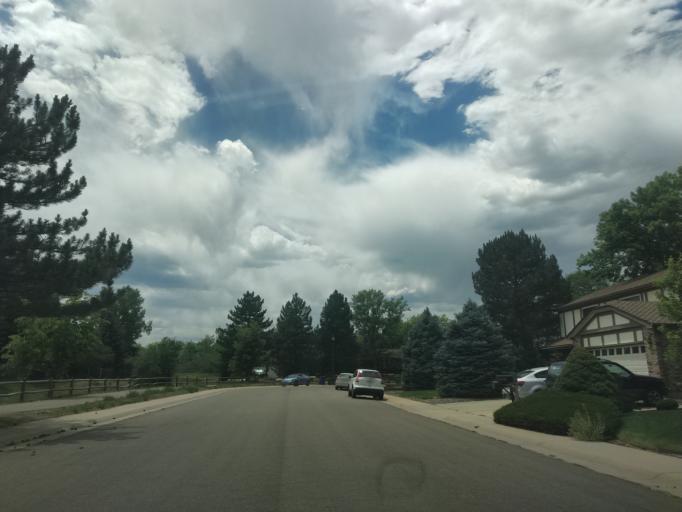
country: US
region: Colorado
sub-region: Jefferson County
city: Lakewood
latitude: 39.6783
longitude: -105.1035
